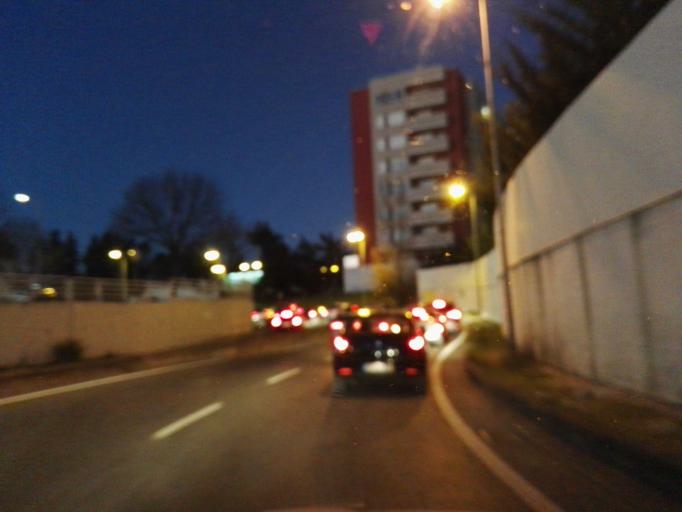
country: PT
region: Lisbon
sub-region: Odivelas
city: Pontinha
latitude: 38.7551
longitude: -9.1828
